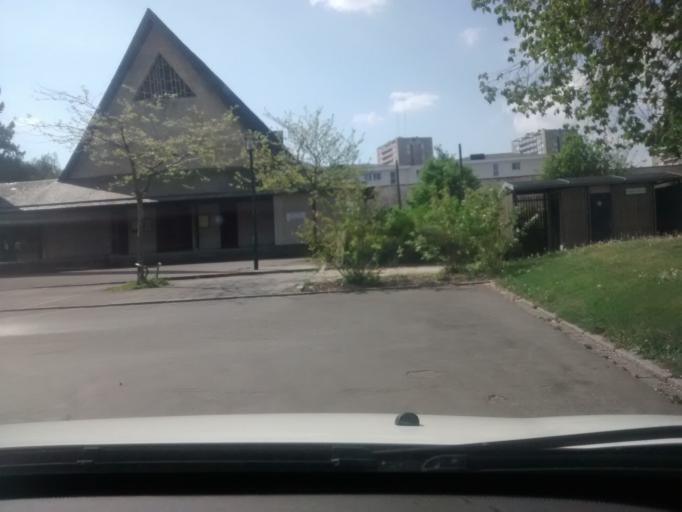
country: FR
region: Brittany
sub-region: Departement d'Ille-et-Vilaine
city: Rennes
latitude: 48.1305
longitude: -1.6596
